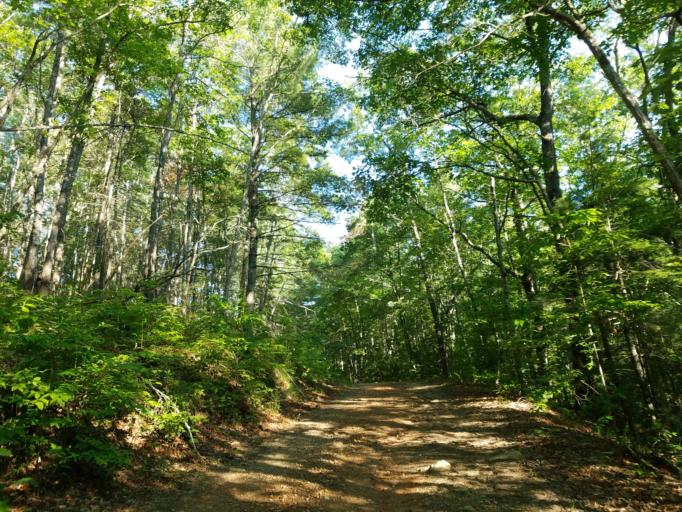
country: US
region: Georgia
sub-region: Fannin County
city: Blue Ridge
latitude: 34.8018
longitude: -84.1802
